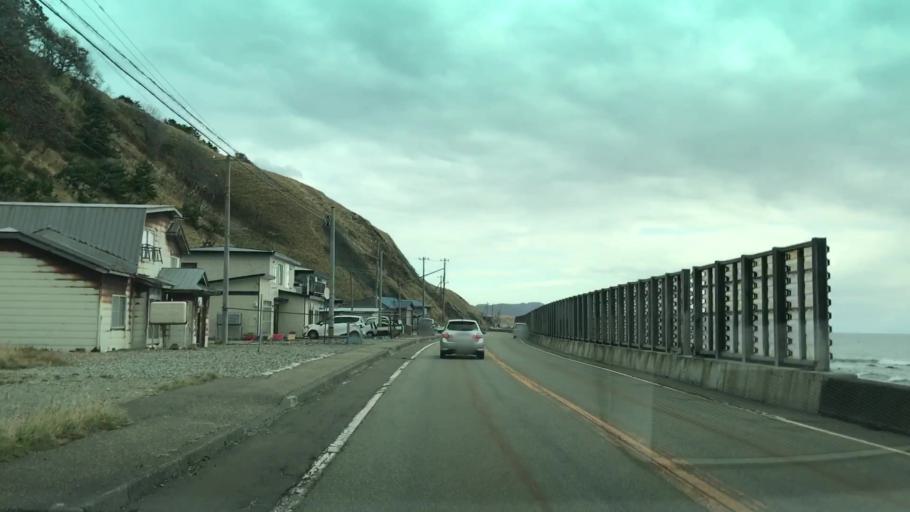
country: JP
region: Hokkaido
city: Shizunai-furukawacho
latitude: 42.0541
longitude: 143.0847
